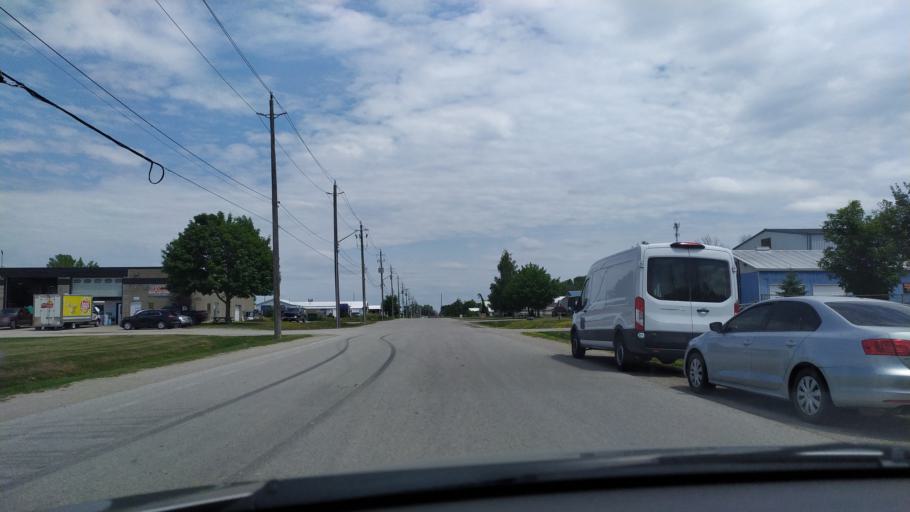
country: CA
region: Ontario
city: Stratford
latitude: 43.3518
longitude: -80.9865
